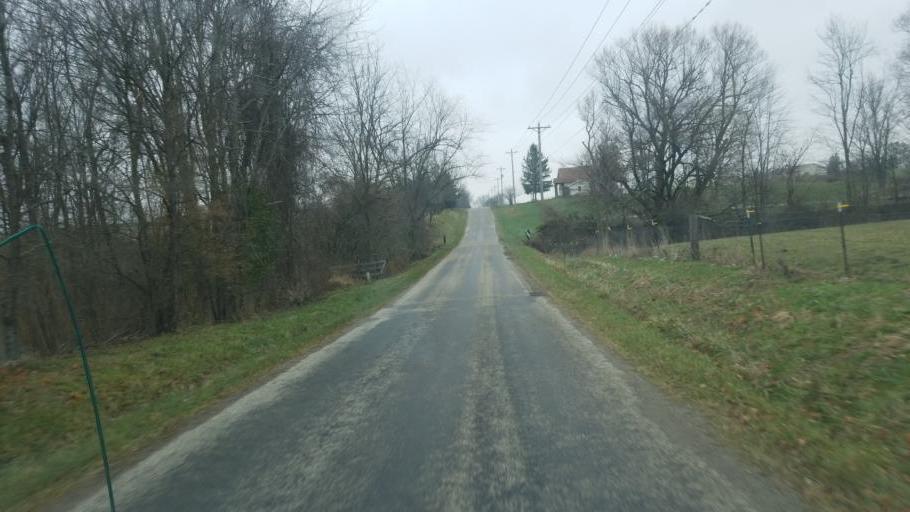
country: US
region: Ohio
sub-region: Huron County
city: New London
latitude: 41.0541
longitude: -82.3264
